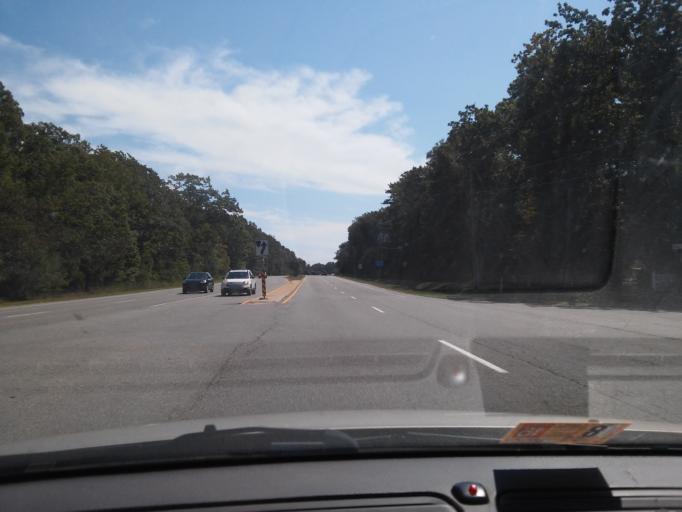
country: US
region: Virginia
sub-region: Chesterfield County
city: Bon Air
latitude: 37.5342
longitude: -77.6340
